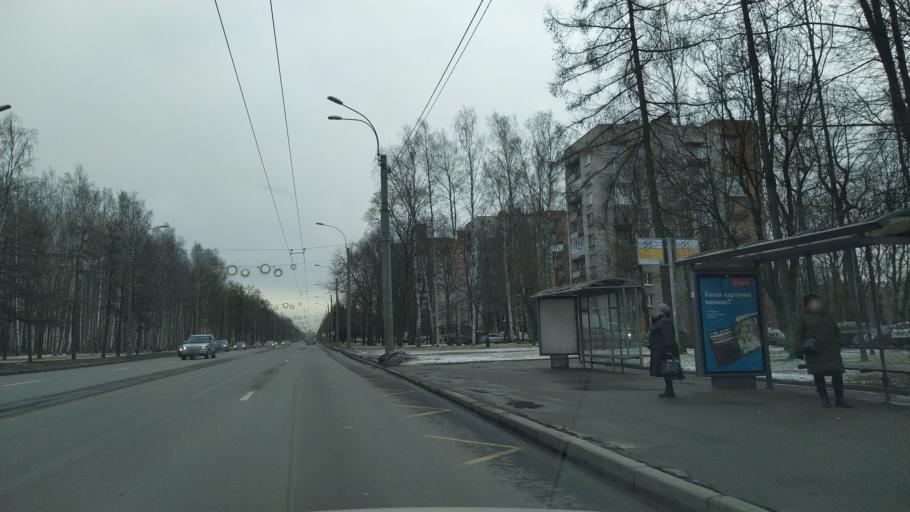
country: RU
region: Leningrad
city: Udel'naya
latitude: 60.0210
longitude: 30.3308
